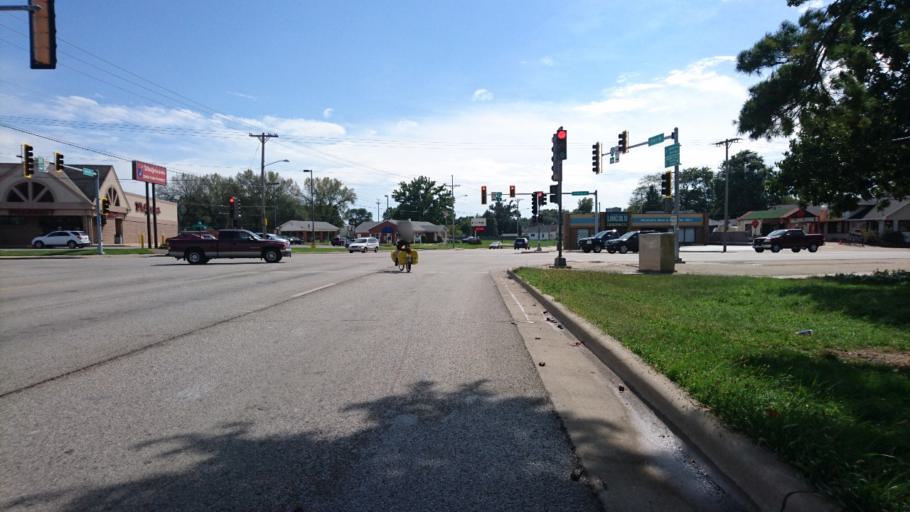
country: US
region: Illinois
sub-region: Sangamon County
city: Grandview
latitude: 39.8315
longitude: -89.6364
